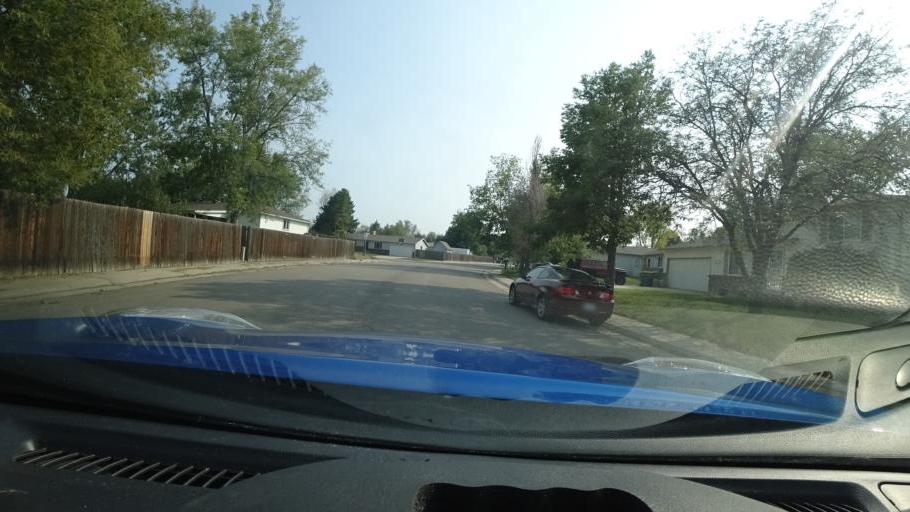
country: US
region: Colorado
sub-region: Adams County
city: Aurora
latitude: 39.6653
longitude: -104.7986
